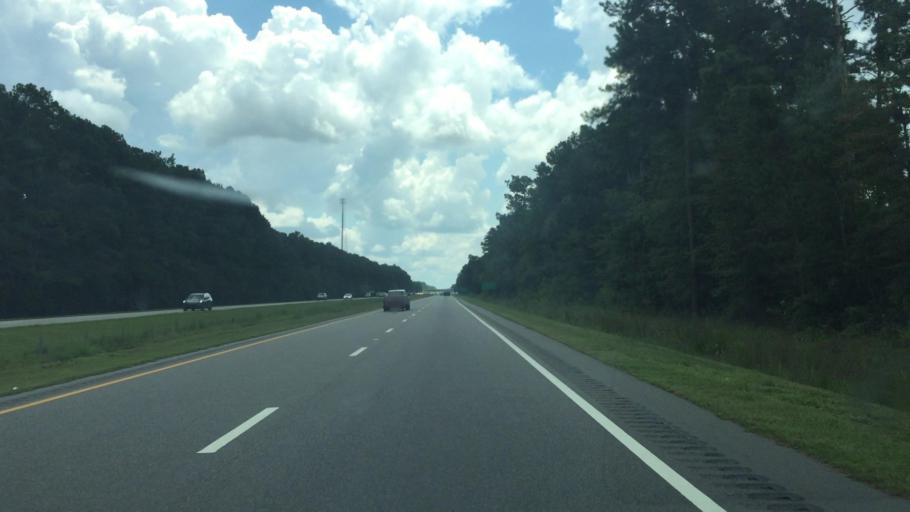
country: US
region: North Carolina
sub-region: Columbus County
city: Chadbourn
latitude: 34.3729
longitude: -78.8441
